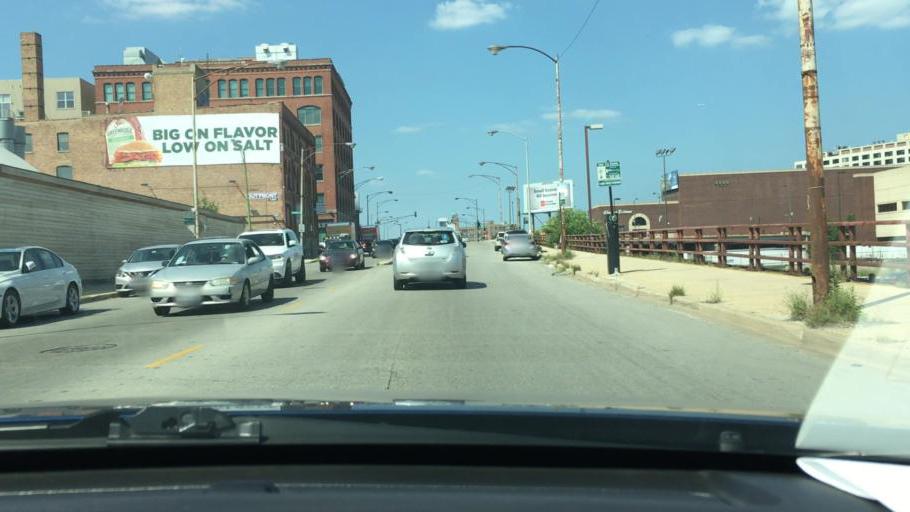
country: US
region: Illinois
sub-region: Cook County
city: Chicago
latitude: 41.8946
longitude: -87.6480
